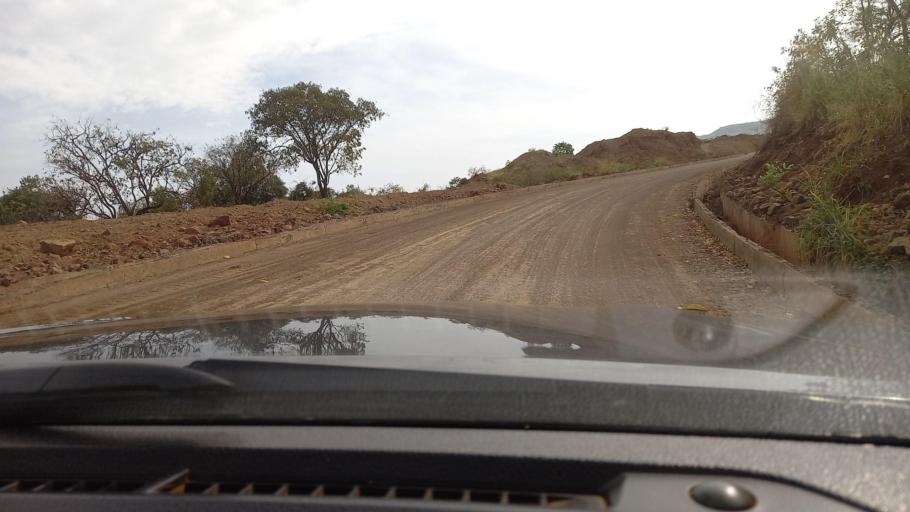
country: ET
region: Southern Nations, Nationalities, and People's Region
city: Mizan Teferi
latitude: 6.1933
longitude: 35.6836
